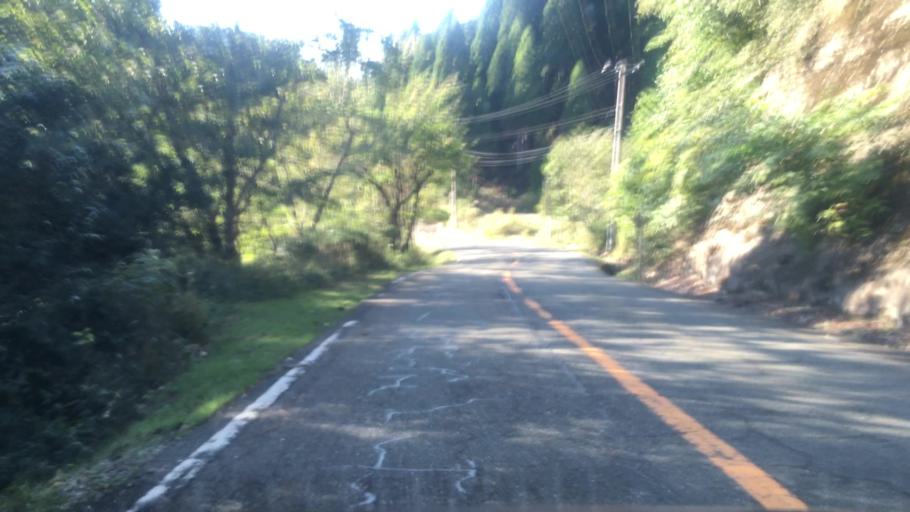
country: JP
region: Hyogo
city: Toyooka
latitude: 35.6202
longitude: 134.8700
